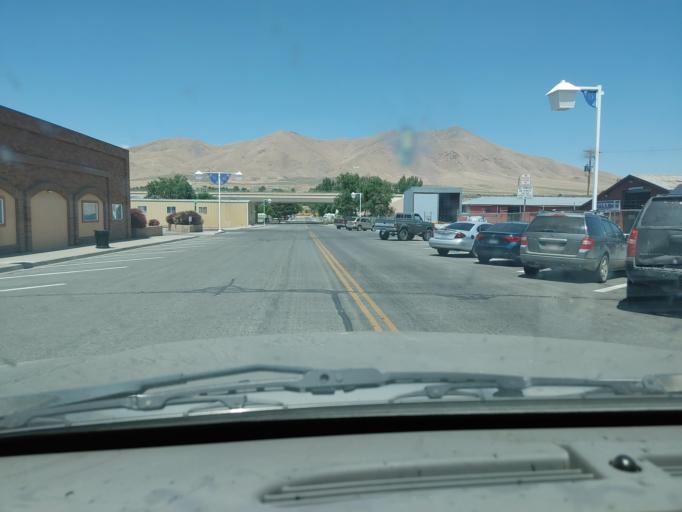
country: US
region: Nevada
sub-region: Humboldt County
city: Winnemucca
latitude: 40.9747
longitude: -117.7366
